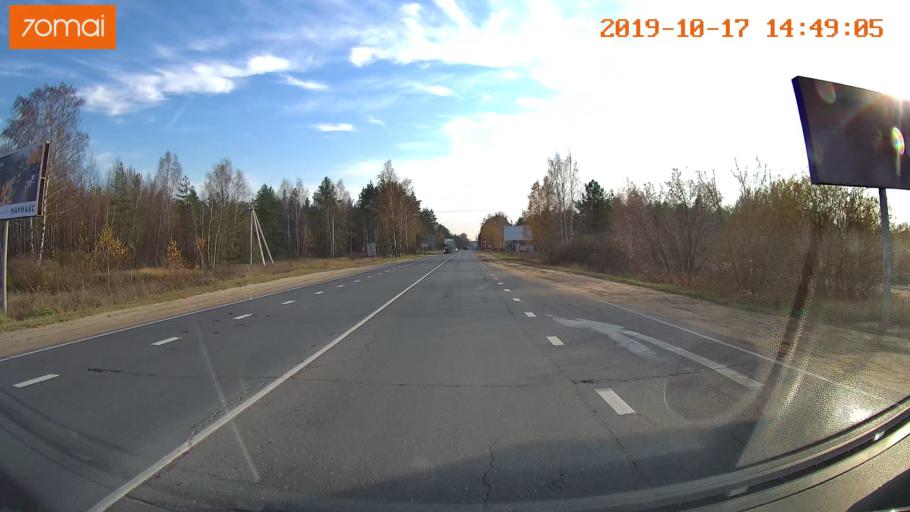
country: RU
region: Rjazan
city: Polyany
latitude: 54.7516
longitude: 39.8388
